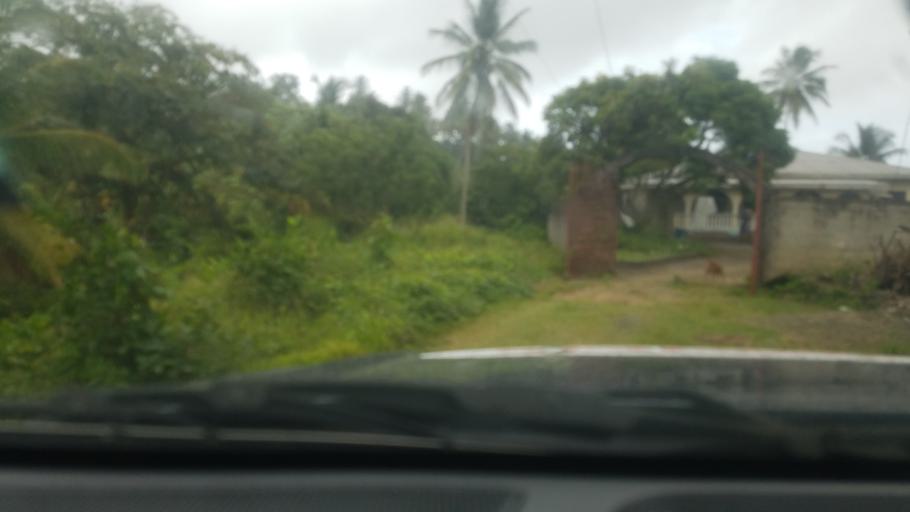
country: LC
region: Micoud Quarter
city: Micoud
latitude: 13.8017
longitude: -60.9445
